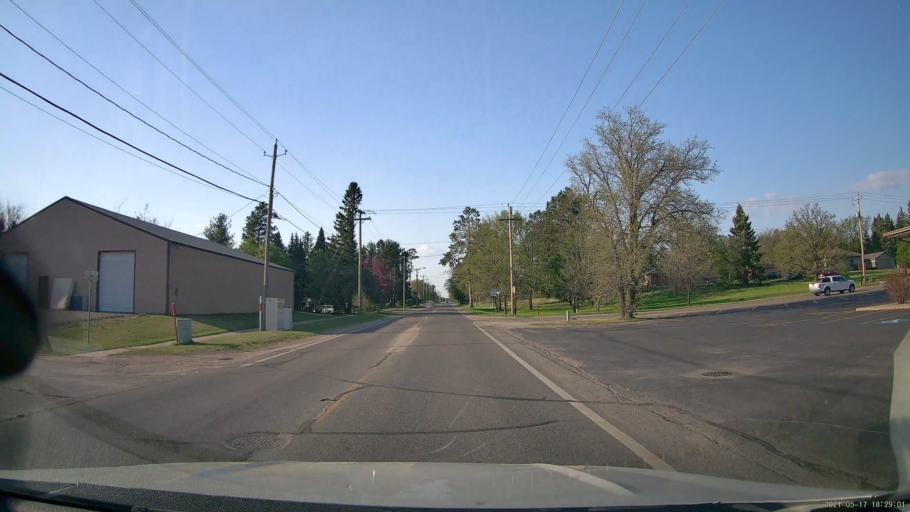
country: US
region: Minnesota
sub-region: Hubbard County
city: Park Rapids
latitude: 46.9226
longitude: -95.0486
